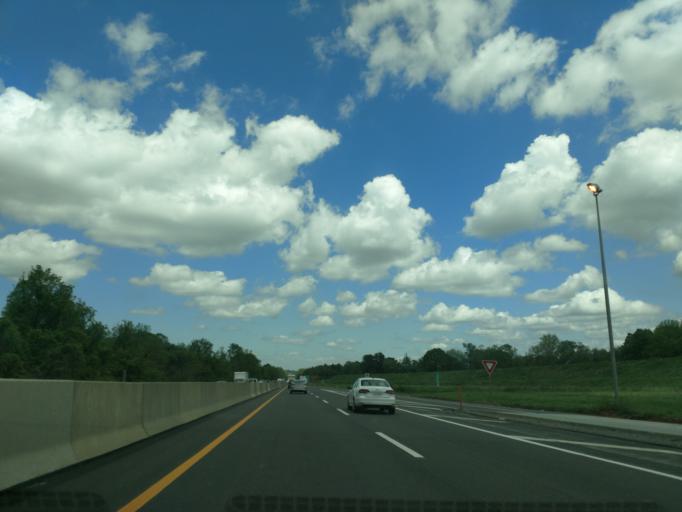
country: US
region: Pennsylvania
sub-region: Chester County
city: Chesterbrook
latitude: 40.0844
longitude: -75.4370
